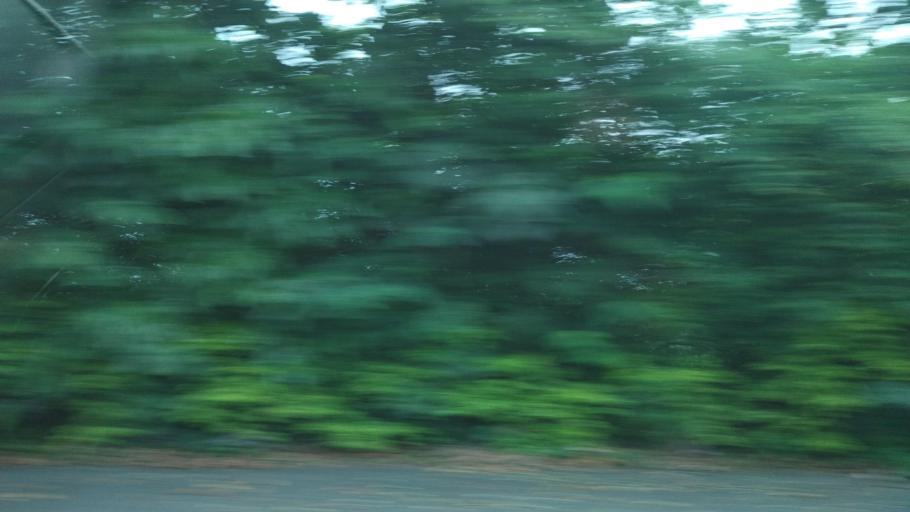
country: TW
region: Taiwan
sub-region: Keelung
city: Keelung
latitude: 25.2202
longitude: 121.6471
